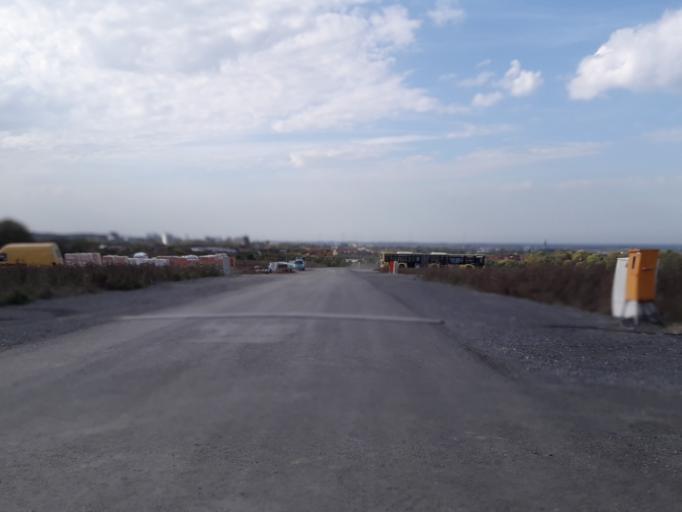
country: DE
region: North Rhine-Westphalia
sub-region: Regierungsbezirk Detmold
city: Paderborn
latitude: 51.7170
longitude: 8.8095
